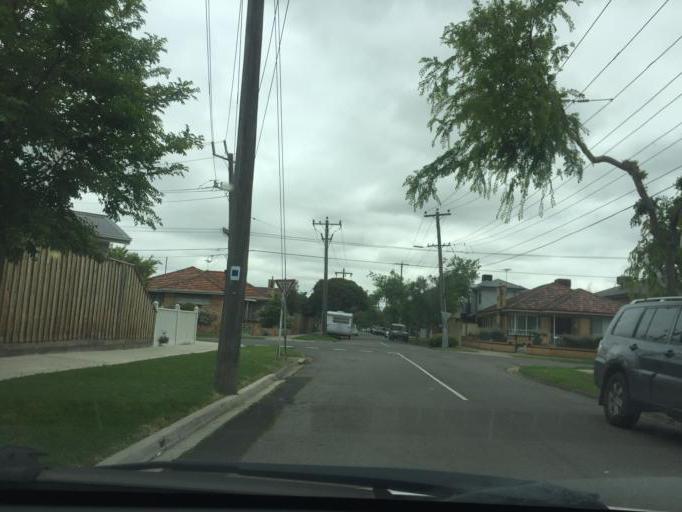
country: AU
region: Victoria
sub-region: Maribyrnong
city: Kingsville
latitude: -37.8153
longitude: 144.8717
